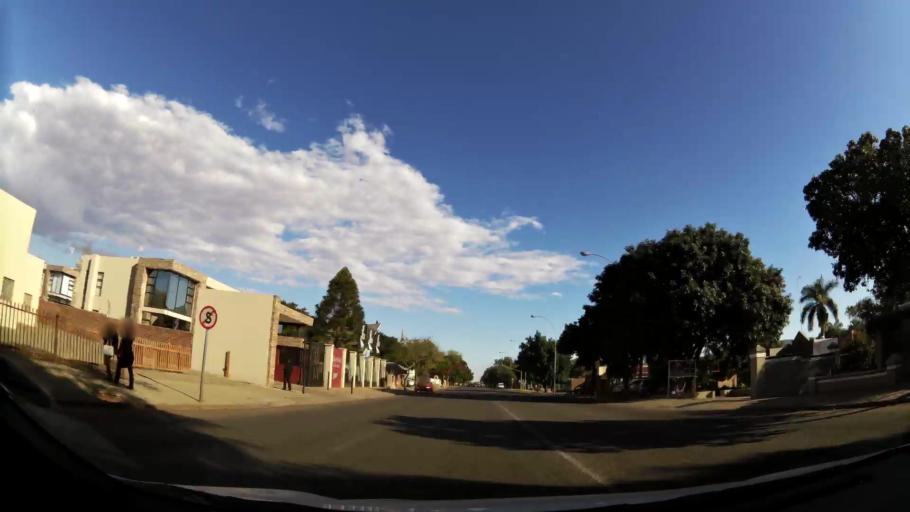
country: ZA
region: Limpopo
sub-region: Waterberg District Municipality
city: Mokopane
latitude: -24.1905
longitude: 29.0104
